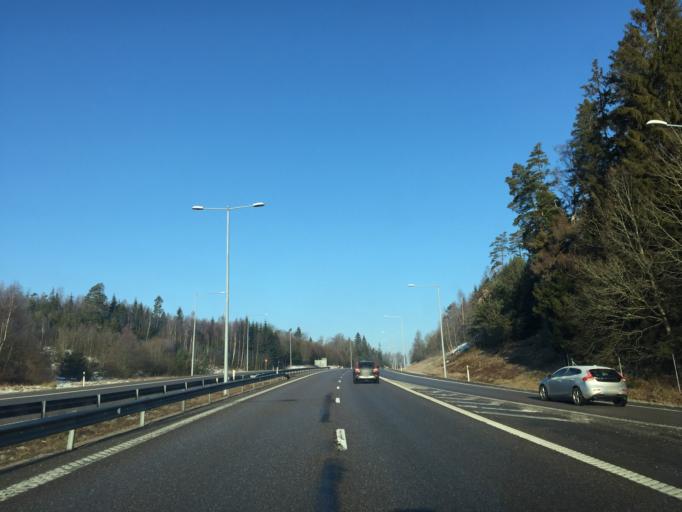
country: SE
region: Vaestra Goetaland
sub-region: Uddevalla Kommun
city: Ljungskile
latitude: 58.2922
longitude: 11.8678
